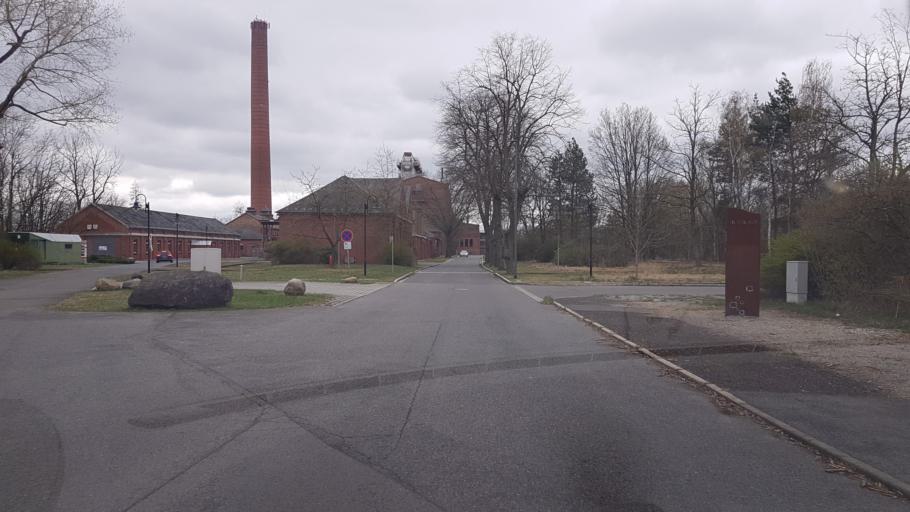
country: DE
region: Saxony
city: Lohsa
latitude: 51.3996
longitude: 14.3271
